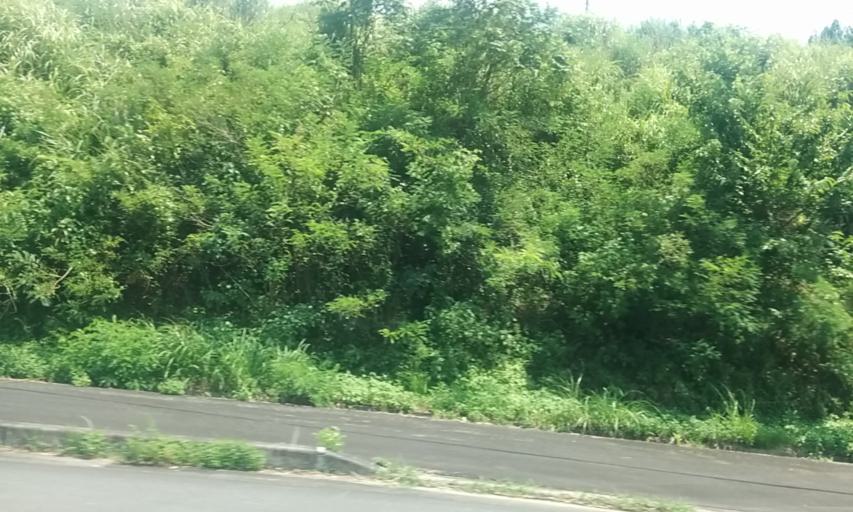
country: JP
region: Kyoto
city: Ayabe
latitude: 35.2200
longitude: 135.2154
